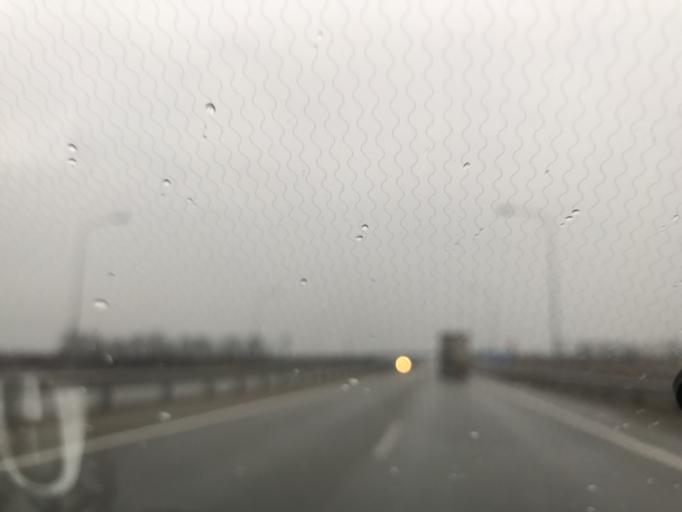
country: RU
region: Krasnodarskiy
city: Krylovskaya
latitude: 46.2977
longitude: 39.8174
